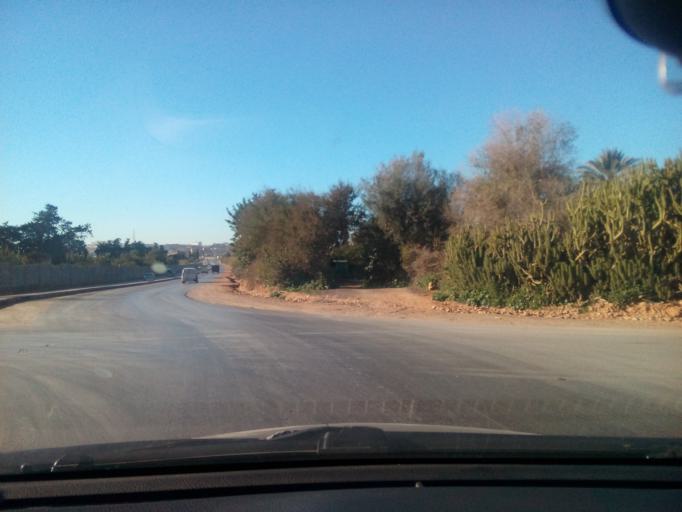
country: DZ
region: Mostaganem
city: Mostaganem
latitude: 35.9174
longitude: 0.1322
